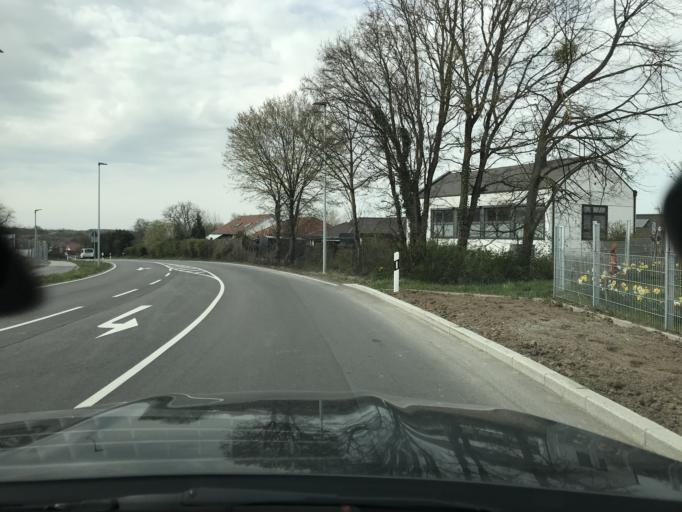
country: DE
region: Baden-Wuerttemberg
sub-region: Regierungsbezirk Stuttgart
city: Burgstetten
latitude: 48.9243
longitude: 9.3748
